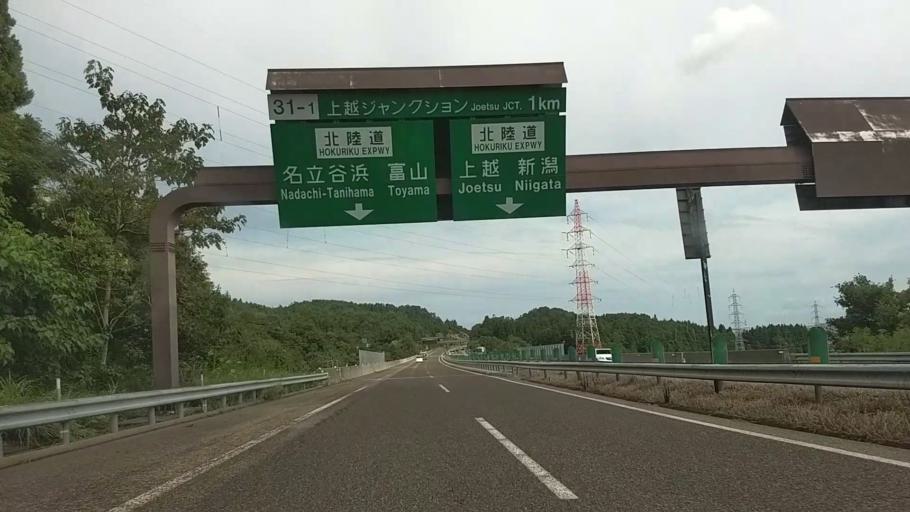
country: JP
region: Niigata
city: Joetsu
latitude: 37.1277
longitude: 138.2125
